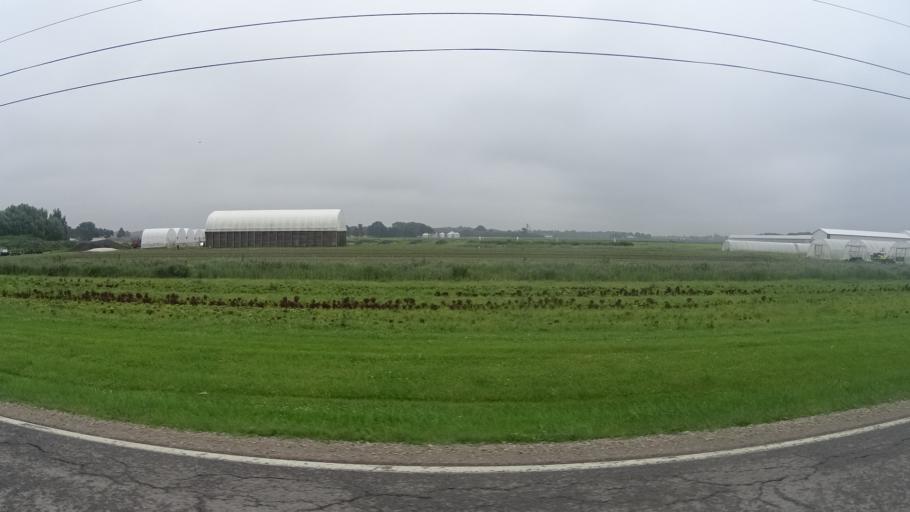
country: US
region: Ohio
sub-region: Erie County
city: Milan
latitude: 41.3586
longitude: -82.6078
